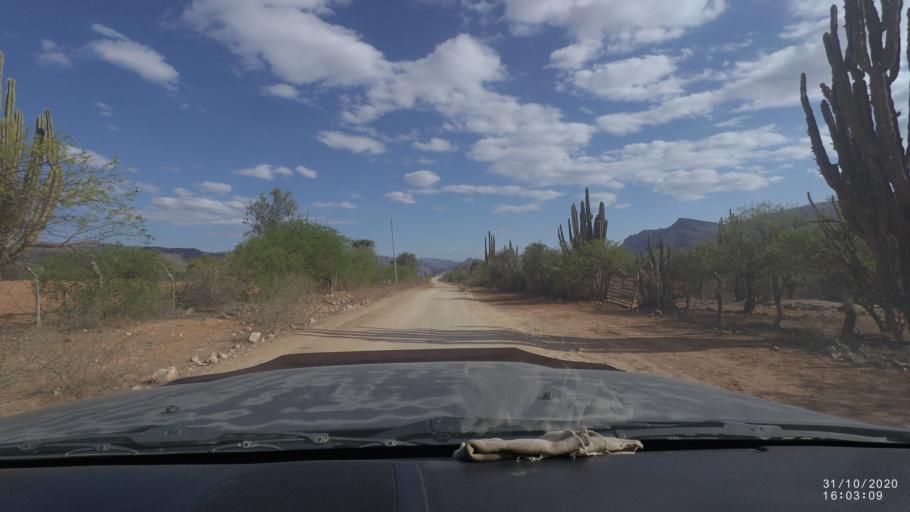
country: BO
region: Chuquisaca
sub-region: Provincia Zudanez
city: Mojocoya
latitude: -18.3497
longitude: -64.6539
